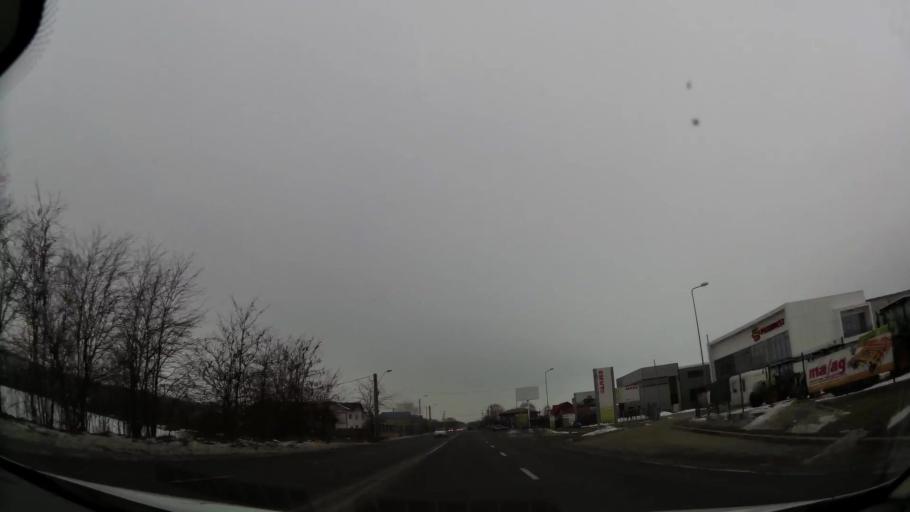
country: RO
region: Ilfov
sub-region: Comuna Buftea
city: Buciumeni
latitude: 44.5302
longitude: 25.9427
